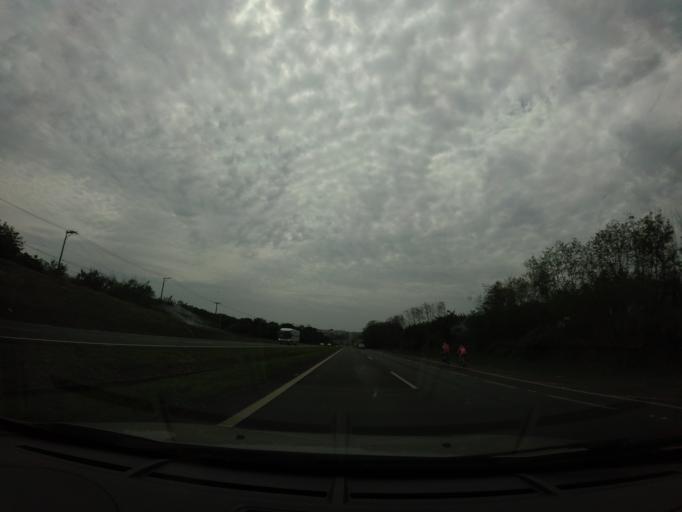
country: BR
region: Sao Paulo
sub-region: Santa Barbara D'Oeste
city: Santa Barbara d'Oeste
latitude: -22.7673
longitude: -47.4301
